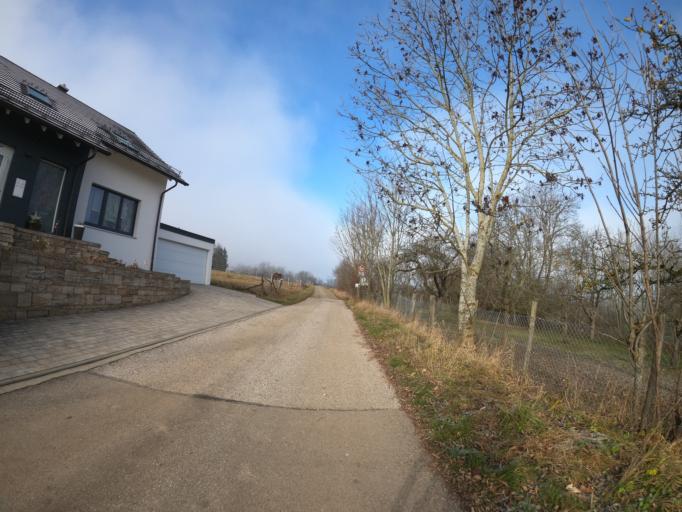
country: DE
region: Baden-Wuerttemberg
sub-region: Regierungsbezirk Stuttgart
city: Bad Uberkingen
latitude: 48.5875
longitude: 9.7582
